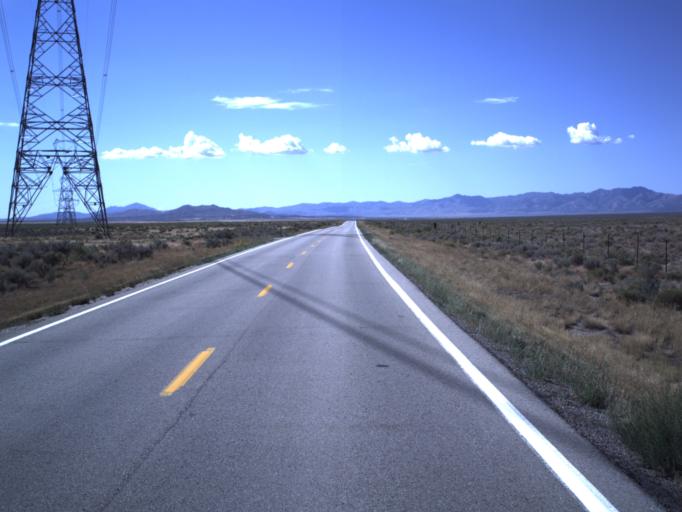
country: US
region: Utah
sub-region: Tooele County
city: Tooele
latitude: 40.2654
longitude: -112.3975
